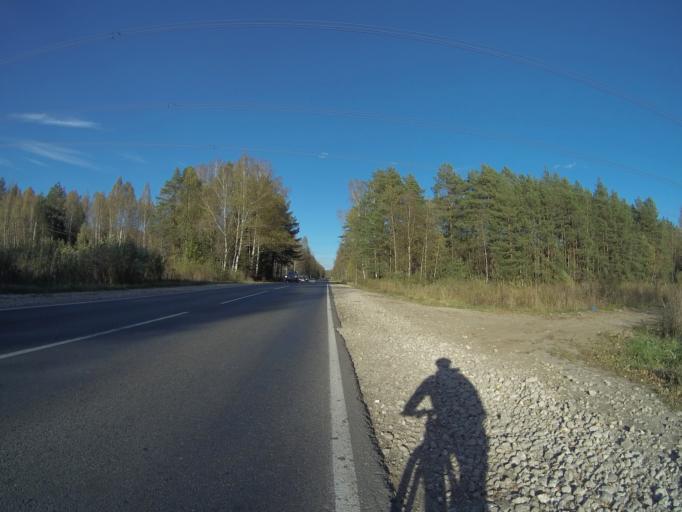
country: RU
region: Vladimir
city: Golovino
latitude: 56.0117
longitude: 40.5733
